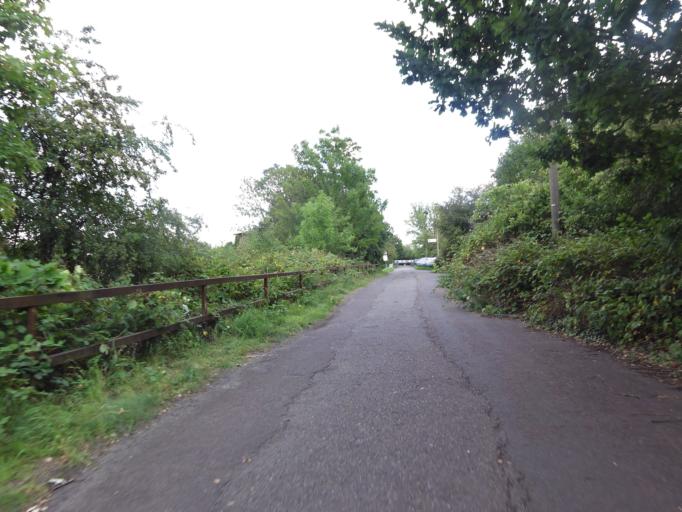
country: DE
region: Saxony
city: Leipzig
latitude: 51.3126
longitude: 12.3165
